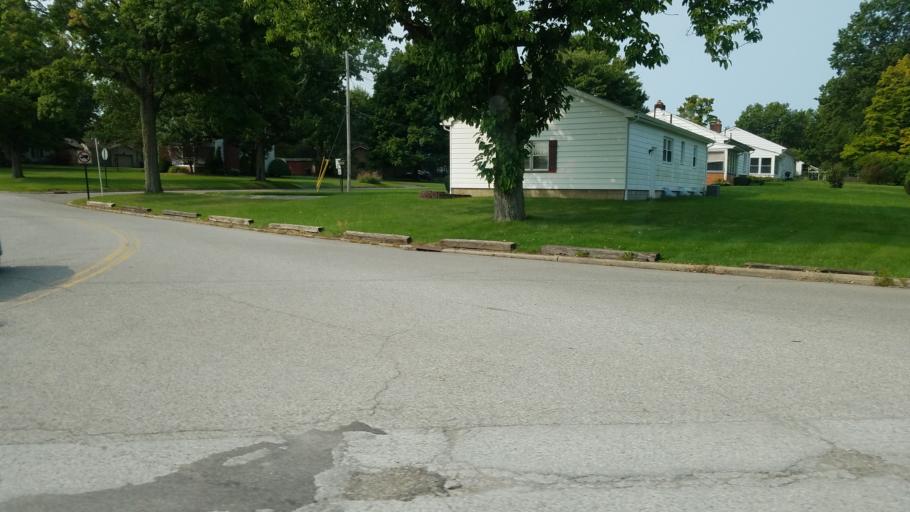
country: US
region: Ohio
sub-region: Mahoning County
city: Struthers
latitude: 41.0535
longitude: -80.6389
